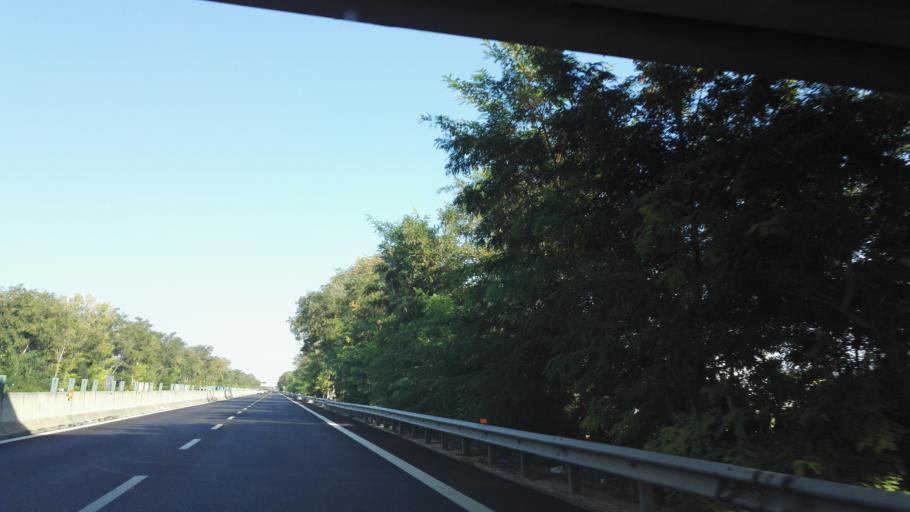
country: IT
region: Apulia
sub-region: Provincia di Bari
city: Mola di Bari
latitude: 41.0408
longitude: 17.1164
